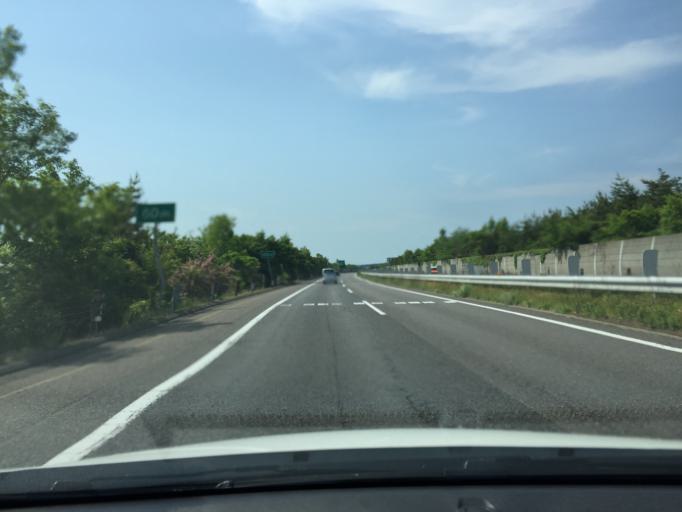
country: JP
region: Fukushima
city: Koriyama
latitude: 37.3802
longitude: 140.3128
